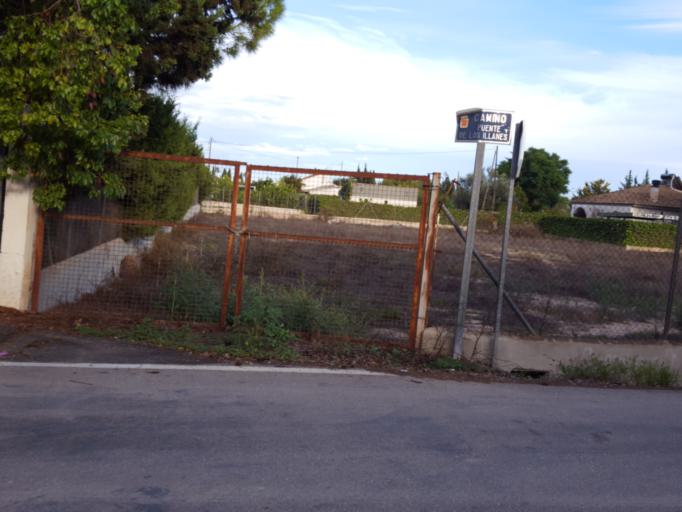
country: ES
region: Murcia
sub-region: Murcia
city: Murcia
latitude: 37.9918
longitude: -1.1695
